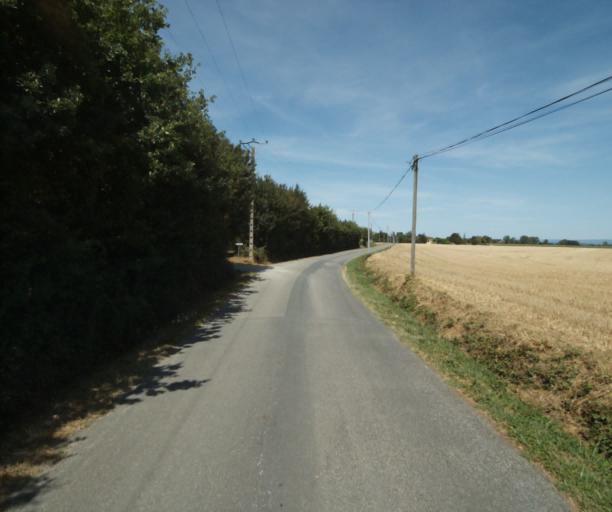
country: FR
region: Midi-Pyrenees
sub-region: Departement de la Haute-Garonne
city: Revel
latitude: 43.4976
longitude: 2.0220
